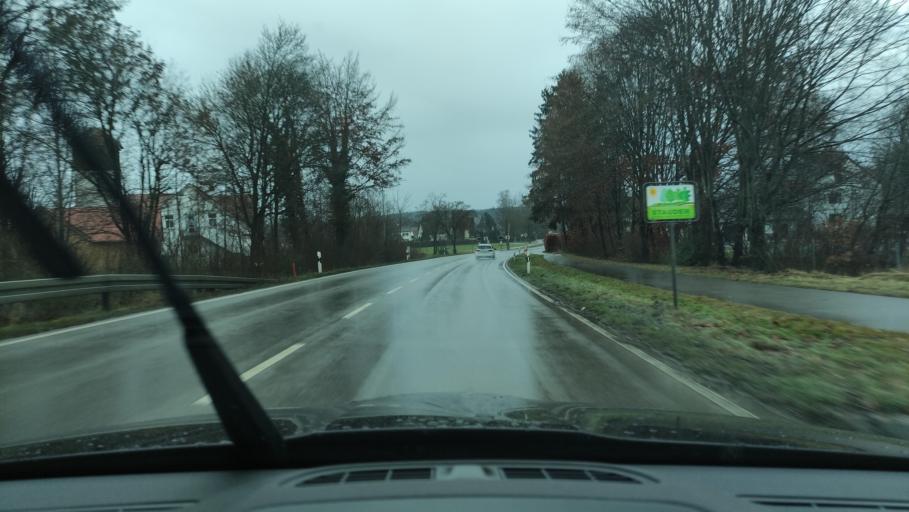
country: DE
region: Bavaria
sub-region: Swabia
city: Gessertshausen
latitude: 48.3289
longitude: 10.7226
